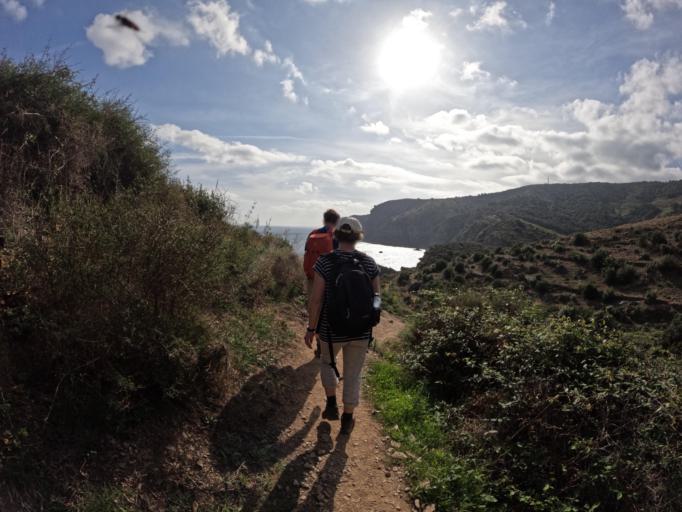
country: FR
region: Languedoc-Roussillon
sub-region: Departement des Pyrenees-Orientales
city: Banyuls de la Marenda
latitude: 42.4750
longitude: 3.1535
